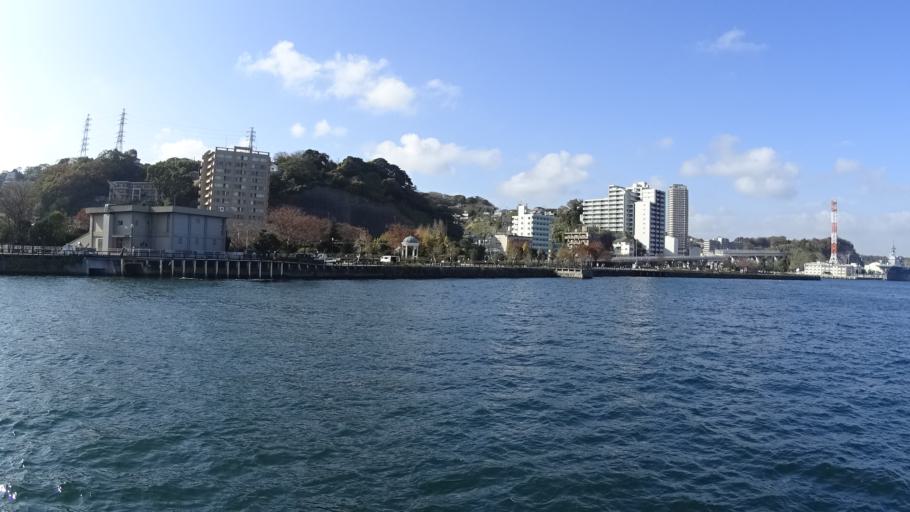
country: JP
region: Kanagawa
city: Yokosuka
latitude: 35.2838
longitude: 139.6610
